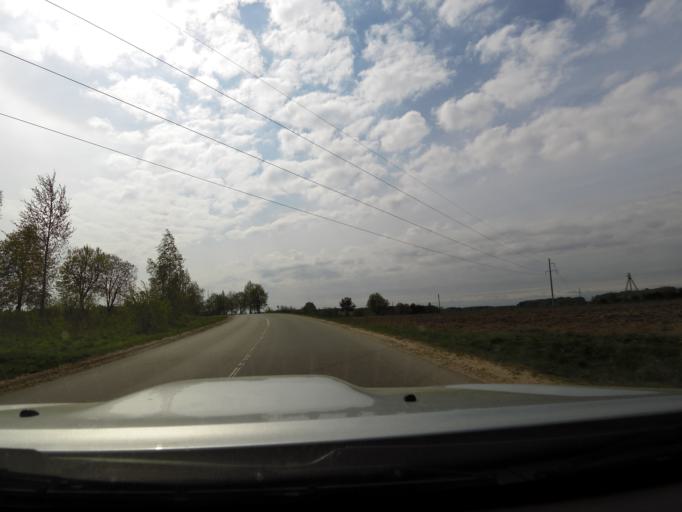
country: LT
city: Baltoji Voke
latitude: 54.5692
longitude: 25.1814
